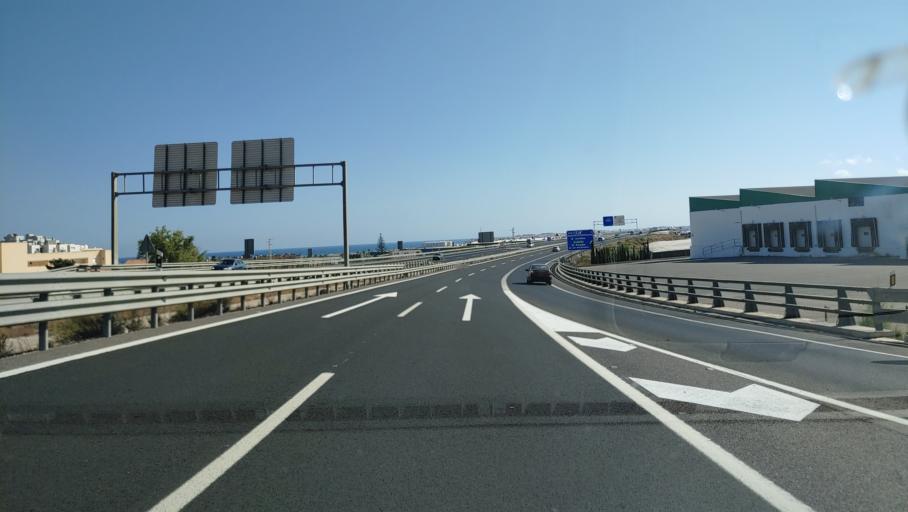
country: ES
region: Andalusia
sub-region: Provincia de Almeria
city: Aguadulce
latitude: 36.8063
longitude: -2.6039
